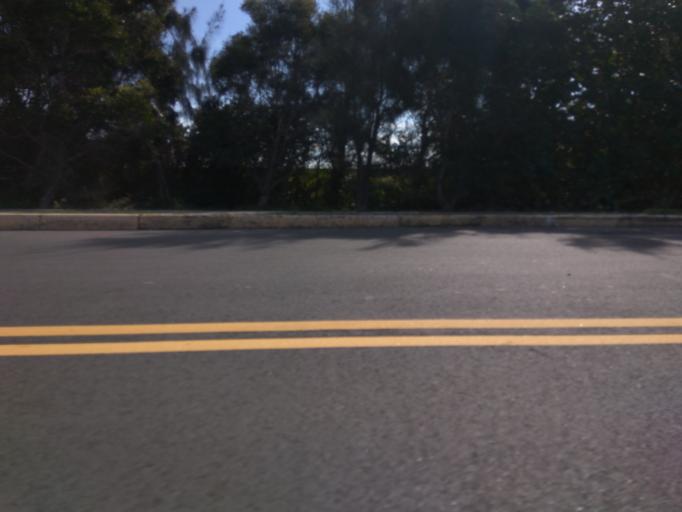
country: TW
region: Taiwan
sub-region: Hsinchu
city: Zhubei
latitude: 25.0414
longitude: 121.0721
